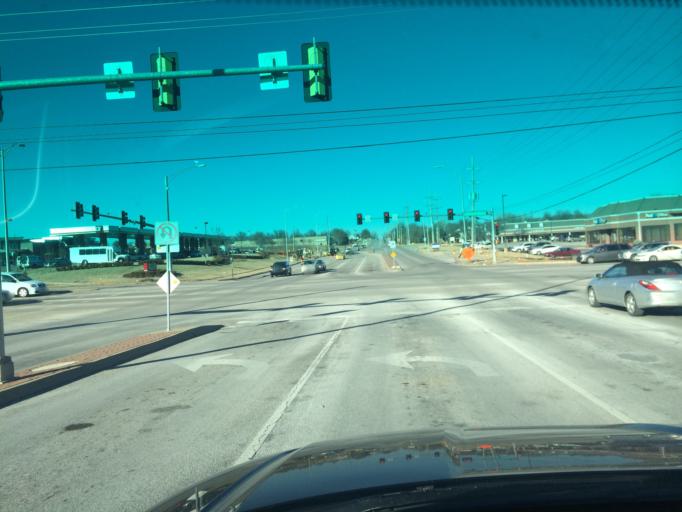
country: US
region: Kansas
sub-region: Johnson County
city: Lenexa
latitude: 38.9270
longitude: -94.7421
